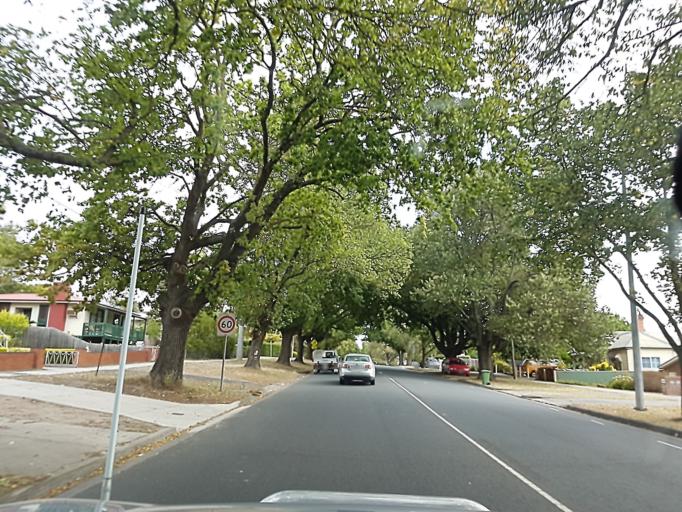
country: AU
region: Victoria
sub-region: Yarra Ranges
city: Lilydale
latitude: -37.7518
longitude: 145.3565
